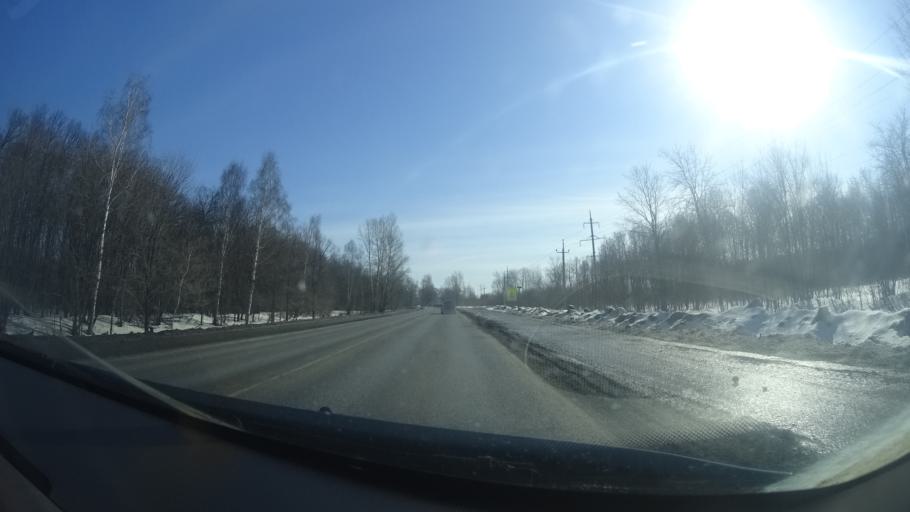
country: RU
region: Bashkortostan
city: Mikhaylovka
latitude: 54.8415
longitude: 55.7902
